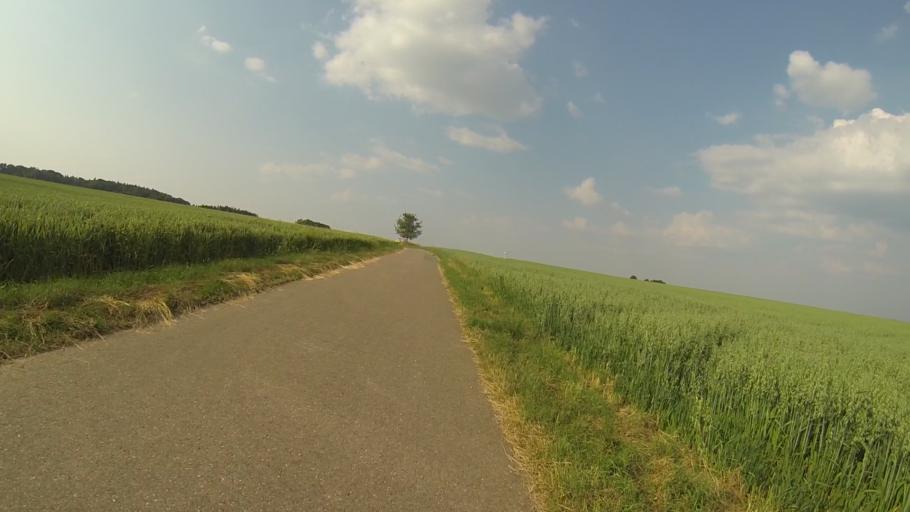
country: DE
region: Bavaria
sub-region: Swabia
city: Neu-Ulm
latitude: 48.4398
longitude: 10.0285
